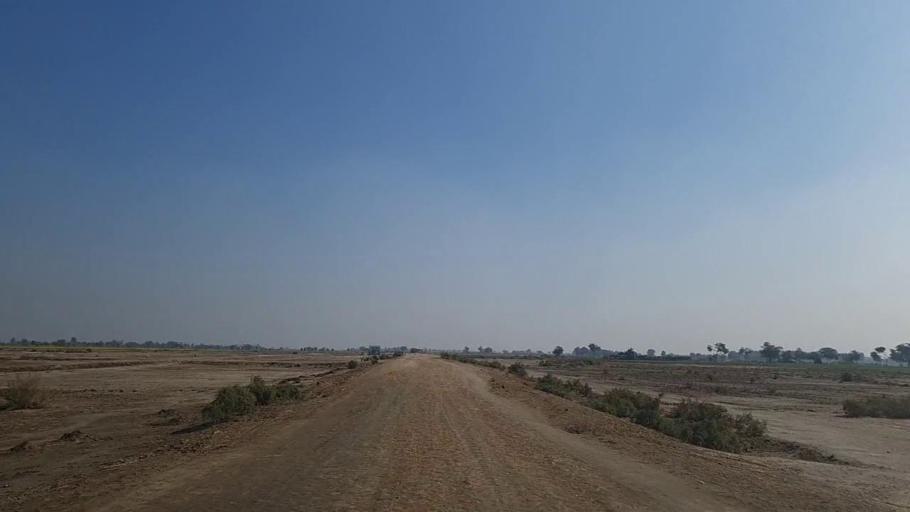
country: PK
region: Sindh
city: Daur
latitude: 26.4664
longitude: 68.3228
